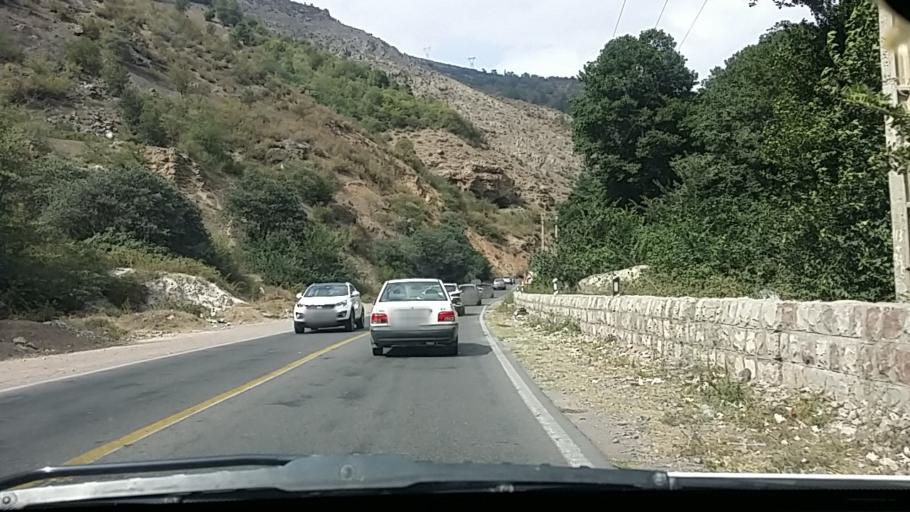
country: IR
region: Mazandaran
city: Chalus
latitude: 36.3637
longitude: 51.2616
